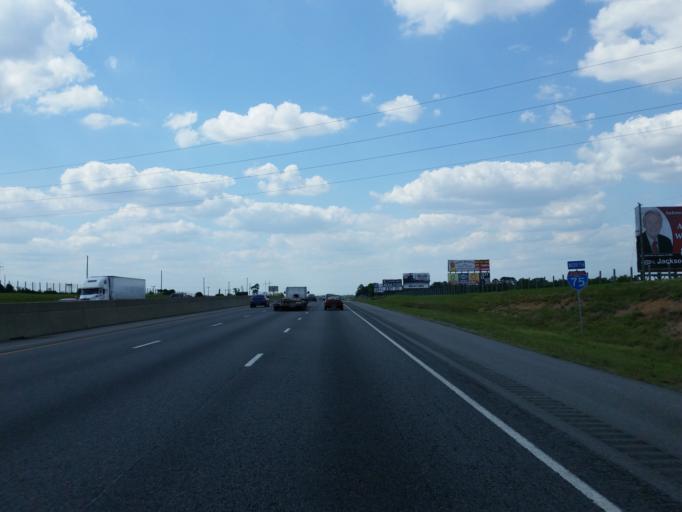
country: US
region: Georgia
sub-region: Tift County
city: Tifton
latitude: 31.5750
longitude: -83.5497
